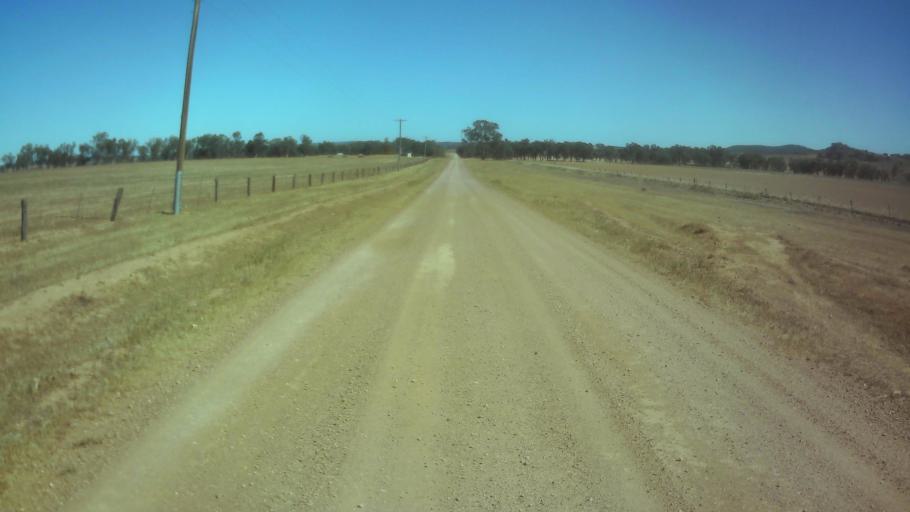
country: AU
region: New South Wales
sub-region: Weddin
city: Grenfell
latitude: -33.9492
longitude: 148.2974
